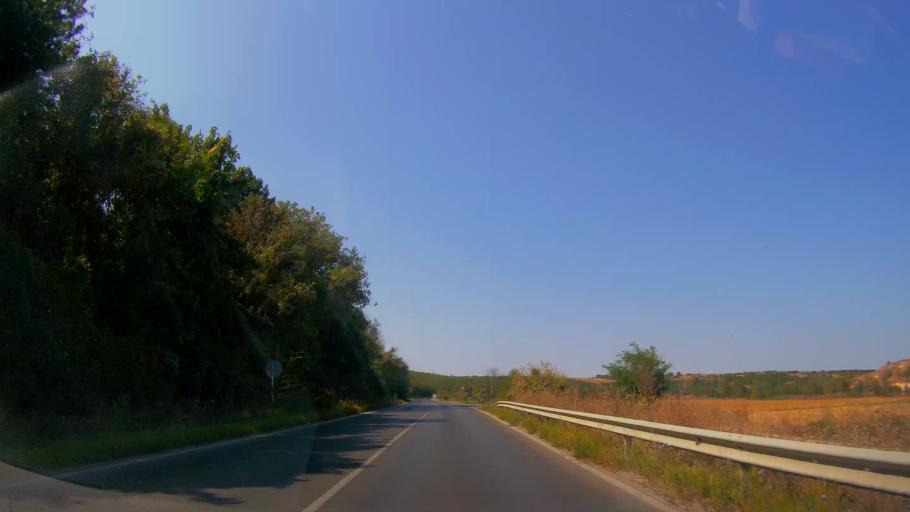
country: BG
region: Razgrad
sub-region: Obshtina Tsar Kaloyan
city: Tsar Kaloyan
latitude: 43.6142
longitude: 26.2192
